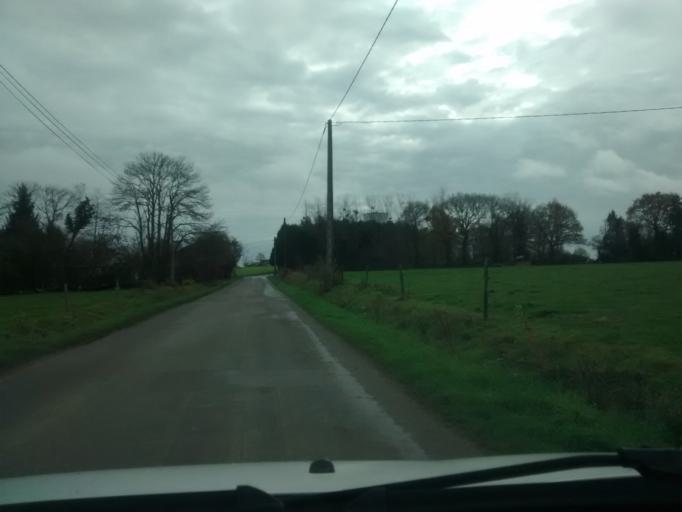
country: FR
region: Brittany
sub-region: Departement d'Ille-et-Vilaine
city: Cesson-Sevigne
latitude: 48.1410
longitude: -1.6038
